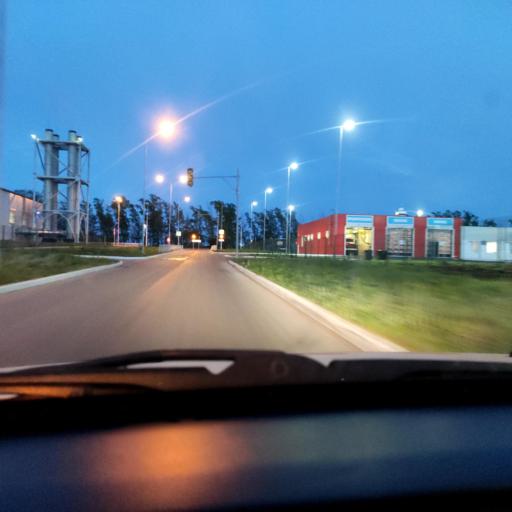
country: RU
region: Samara
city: Samara
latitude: 53.0919
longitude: 50.1585
